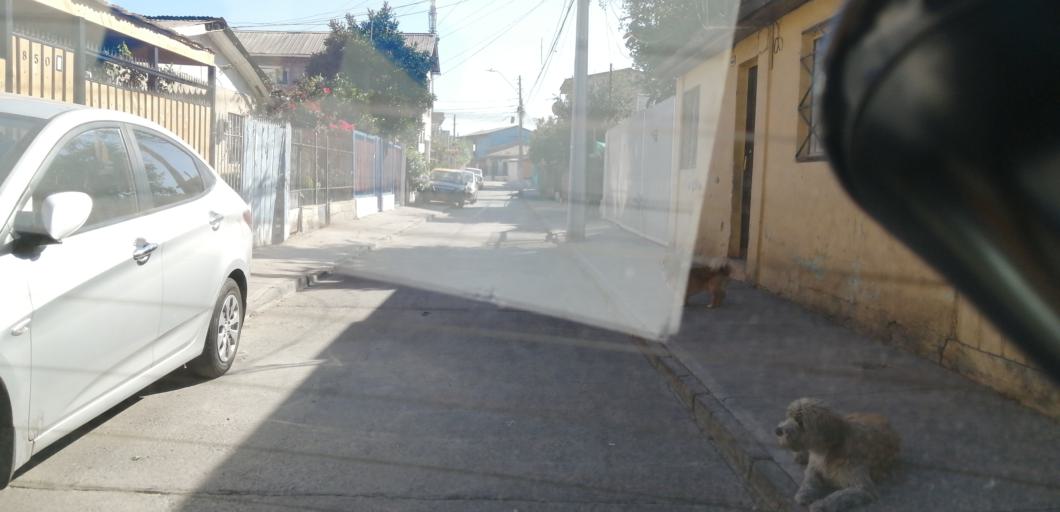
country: CL
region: Santiago Metropolitan
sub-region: Provincia de Santiago
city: Lo Prado
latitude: -33.4404
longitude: -70.7614
